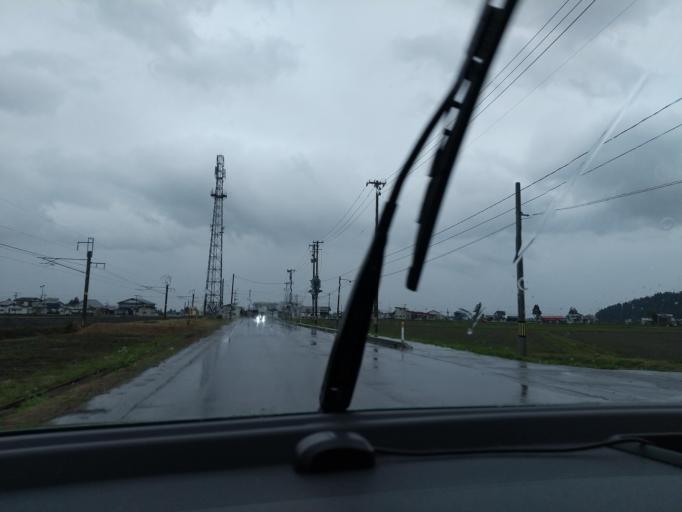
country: JP
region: Akita
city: Yokotemachi
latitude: 39.3710
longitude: 140.5353
